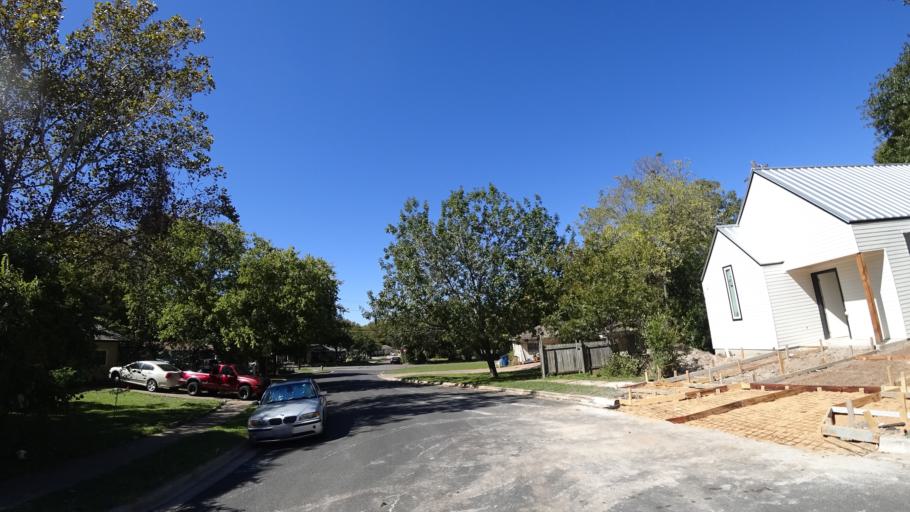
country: US
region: Texas
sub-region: Travis County
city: Austin
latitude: 30.2324
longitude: -97.7714
